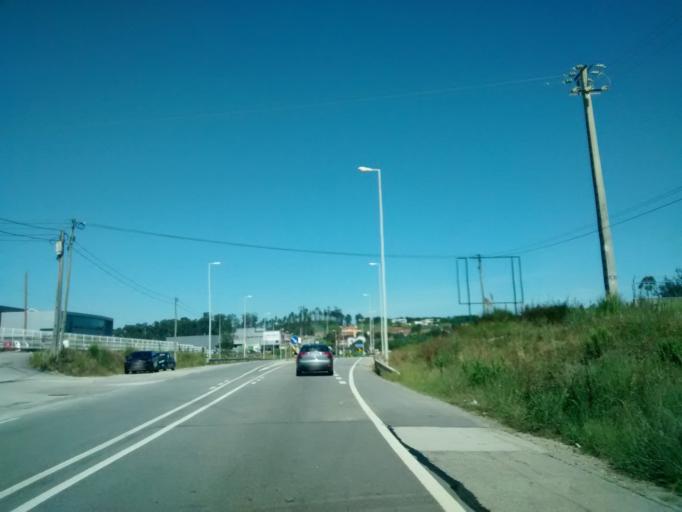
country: PT
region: Aveiro
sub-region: Oliveira do Bairro
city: Oia
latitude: 40.5679
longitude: -8.5673
